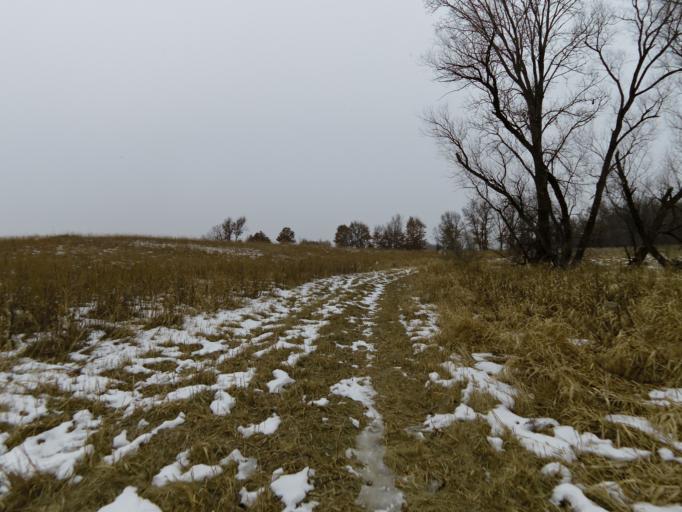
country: US
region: Minnesota
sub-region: Washington County
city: Lake Elmo
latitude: 44.9842
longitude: -92.9122
